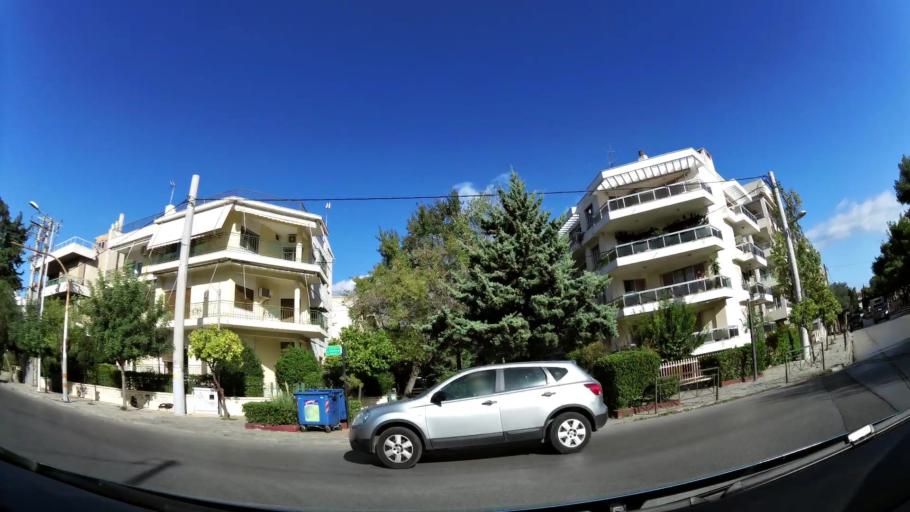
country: GR
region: Attica
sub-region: Nomarchia Athinas
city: Neo Psychiko
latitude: 38.0015
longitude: 23.7809
